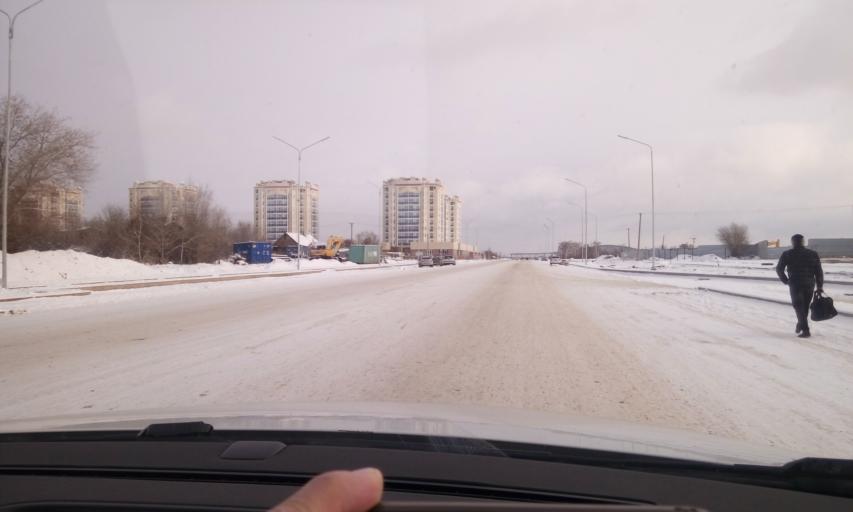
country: KZ
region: Astana Qalasy
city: Astana
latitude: 51.1199
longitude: 71.4995
